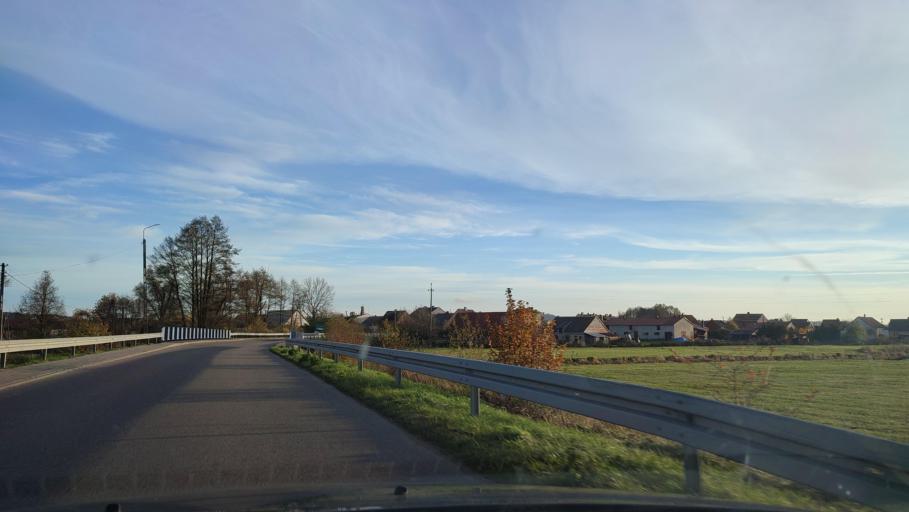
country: PL
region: Masovian Voivodeship
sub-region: Powiat mlawski
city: Dzierzgowo
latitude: 53.3201
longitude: 20.6699
